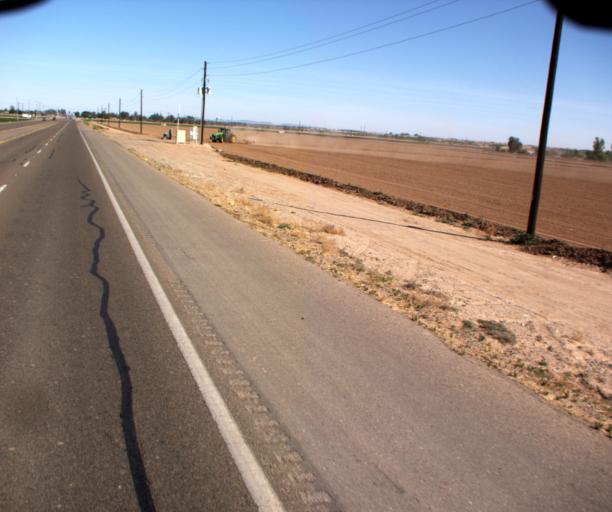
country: US
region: Arizona
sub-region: Yuma County
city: Somerton
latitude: 32.6210
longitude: -114.6497
